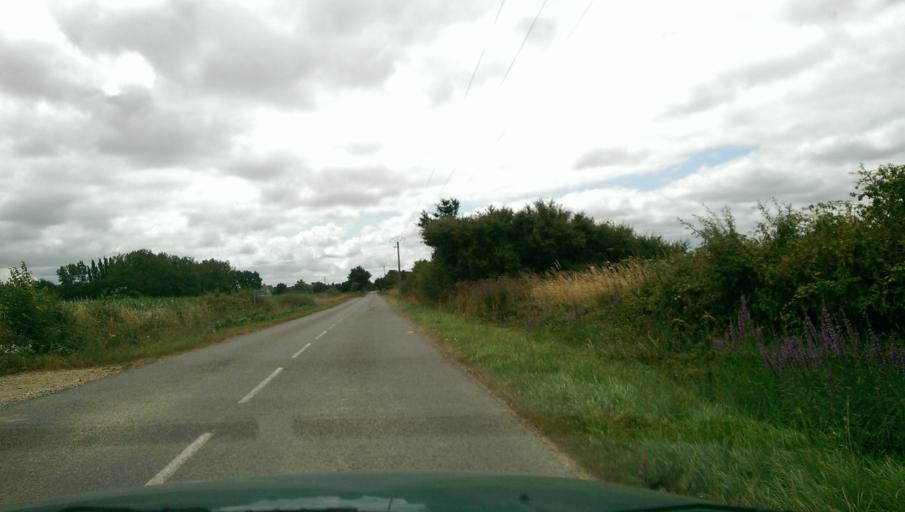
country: FR
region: Pays de la Loire
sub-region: Departement de la Loire-Atlantique
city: La Planche
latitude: 46.9951
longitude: -1.4284
